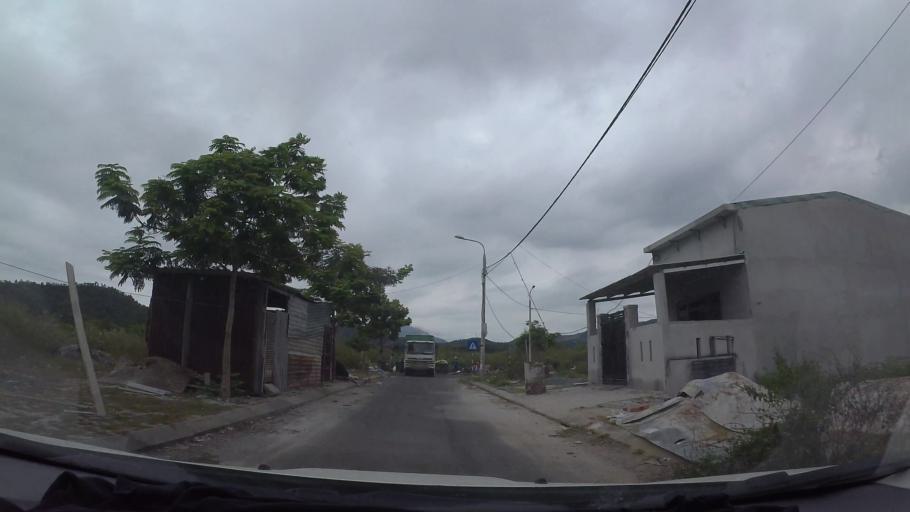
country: VN
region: Da Nang
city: Lien Chieu
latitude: 16.1244
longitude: 108.1158
